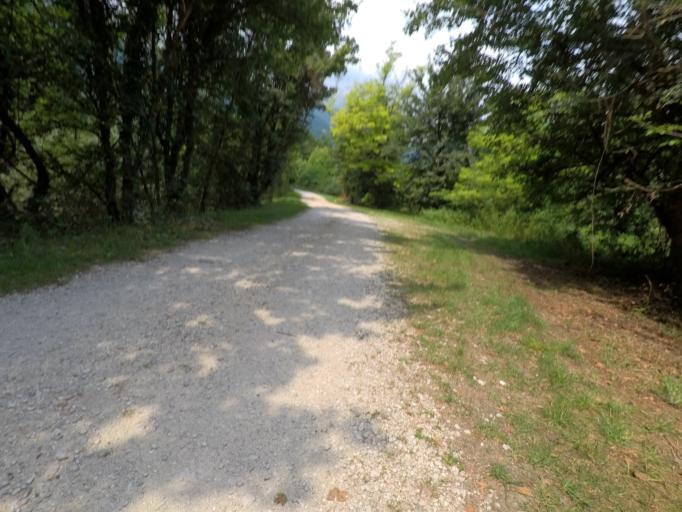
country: IT
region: Friuli Venezia Giulia
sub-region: Provincia di Pordenone
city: Polcenigo
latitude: 46.0245
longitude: 12.4920
